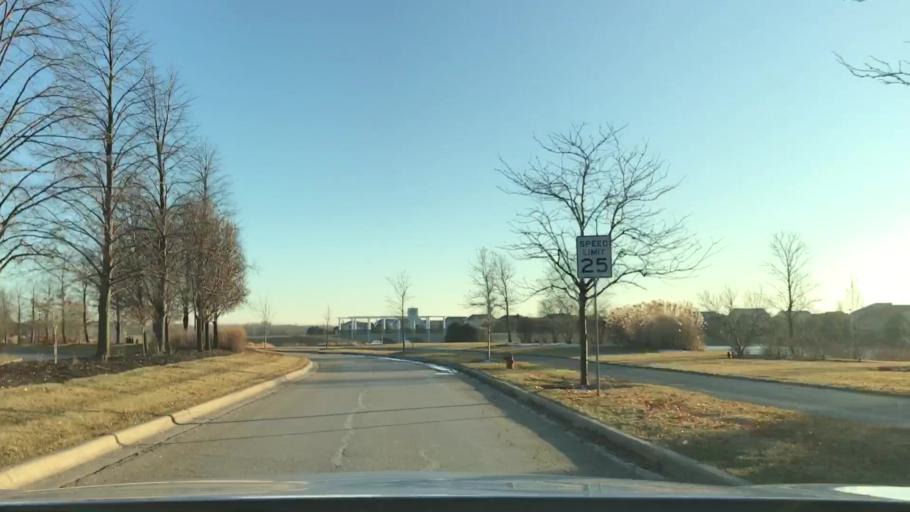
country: US
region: Illinois
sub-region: Kane County
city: Pingree Grove
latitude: 42.0882
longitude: -88.4374
